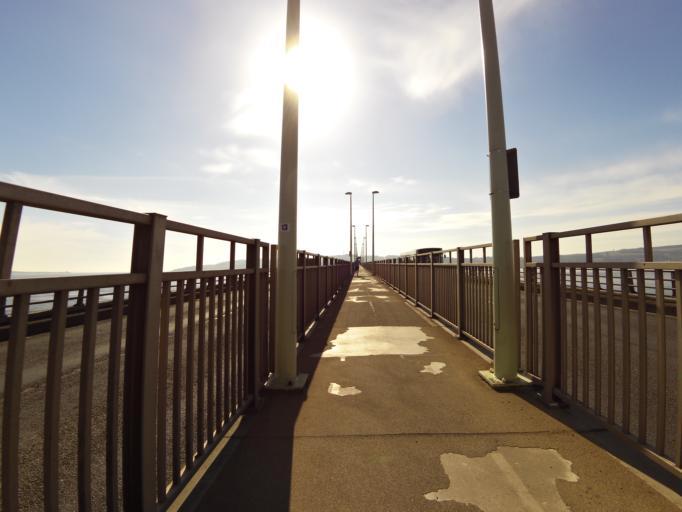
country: GB
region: Scotland
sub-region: Dundee City
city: Dundee
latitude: 56.4570
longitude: -2.9582
